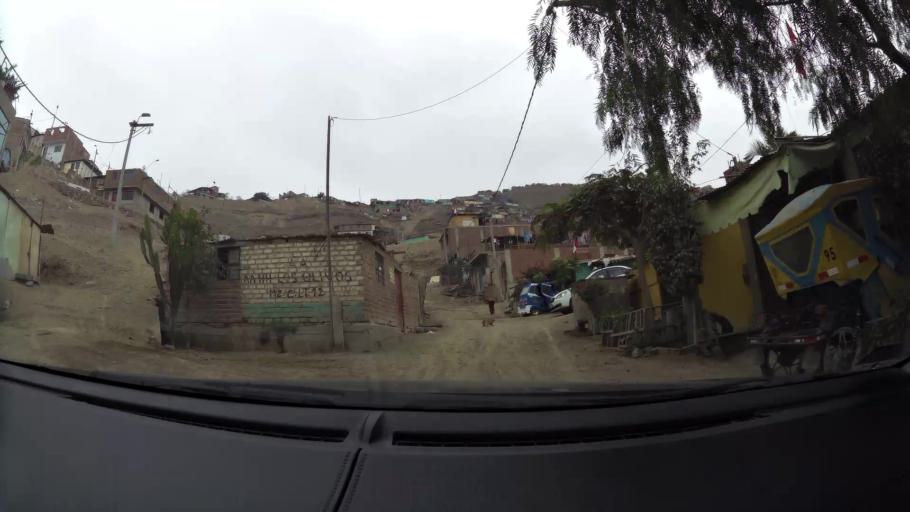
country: PE
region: Lima
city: Ventanilla
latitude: -11.9328
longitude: -77.0904
